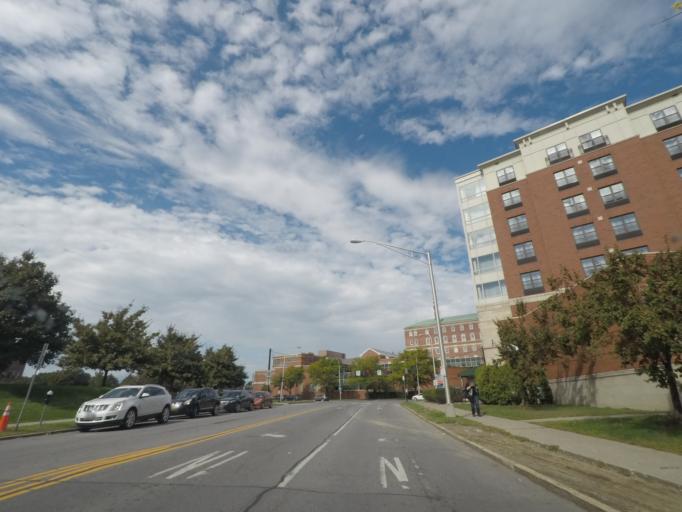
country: US
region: New York
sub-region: Albany County
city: Albany
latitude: 42.6519
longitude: -73.7766
